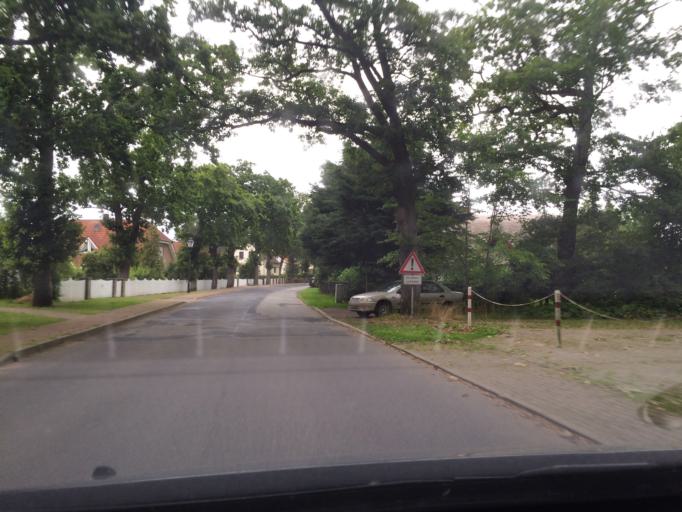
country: DE
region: Mecklenburg-Vorpommern
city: Prohn
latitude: 54.4073
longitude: 13.0144
